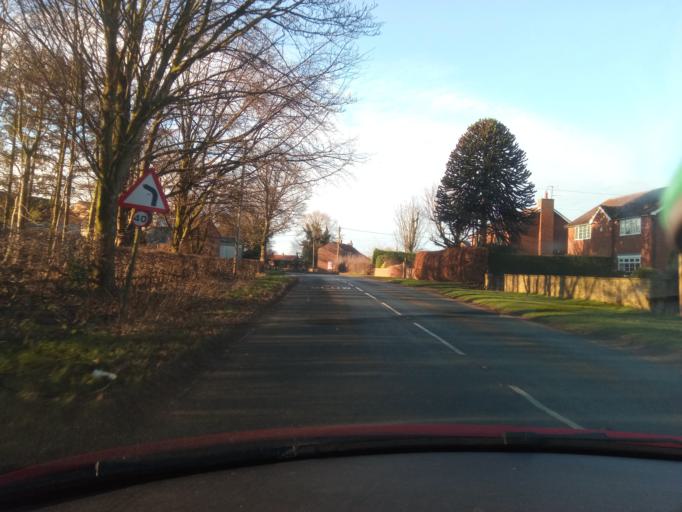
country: GB
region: England
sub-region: North Yorkshire
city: Ripon
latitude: 54.2227
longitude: -1.4645
